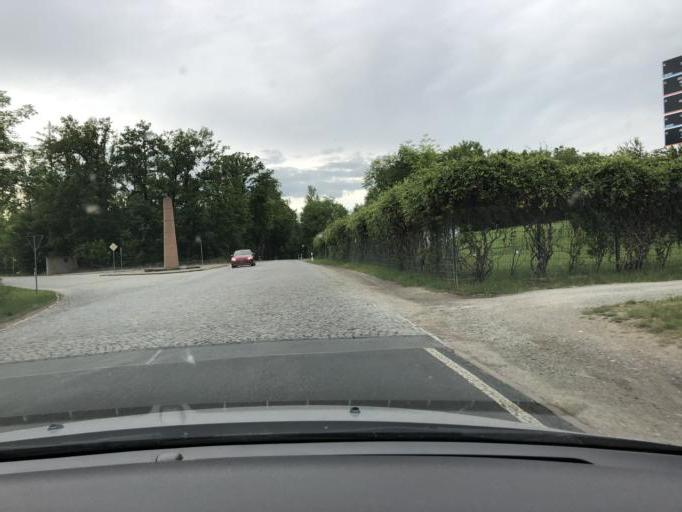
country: DE
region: Thuringia
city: Kleinobringen
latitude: 51.0165
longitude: 11.3039
